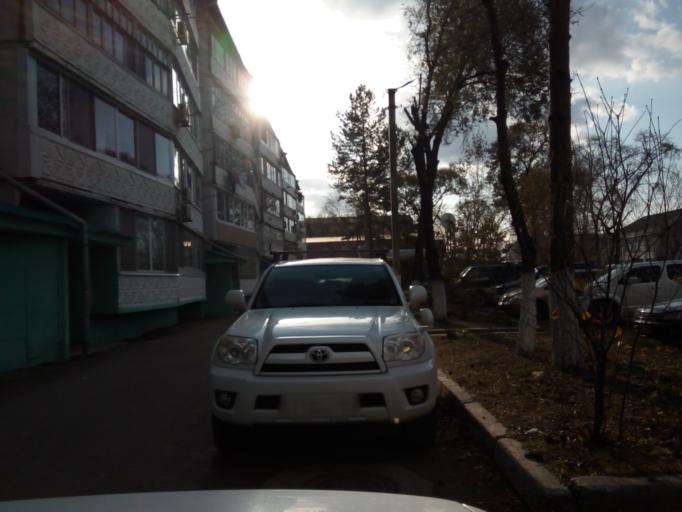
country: RU
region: Primorskiy
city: Dal'nerechensk
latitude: 45.9338
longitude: 133.7313
